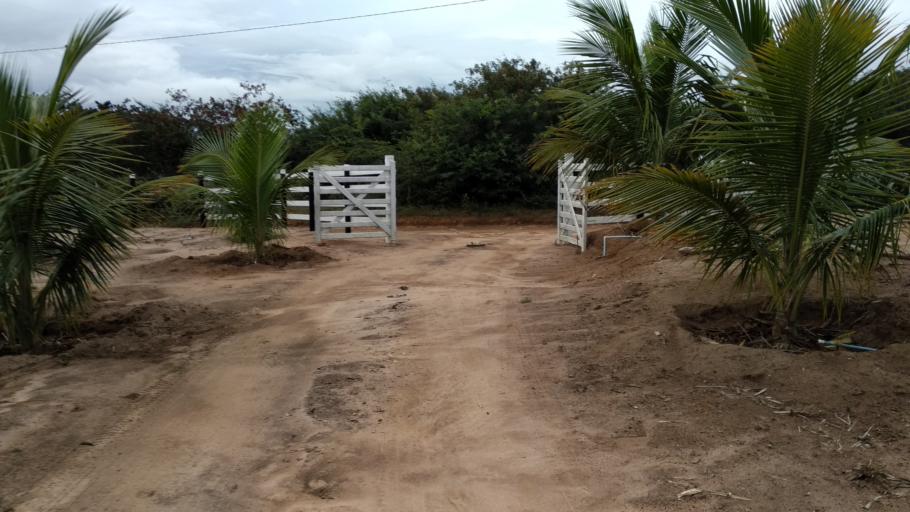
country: BR
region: Bahia
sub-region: Caetite
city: Caetite
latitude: -13.9764
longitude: -42.5174
